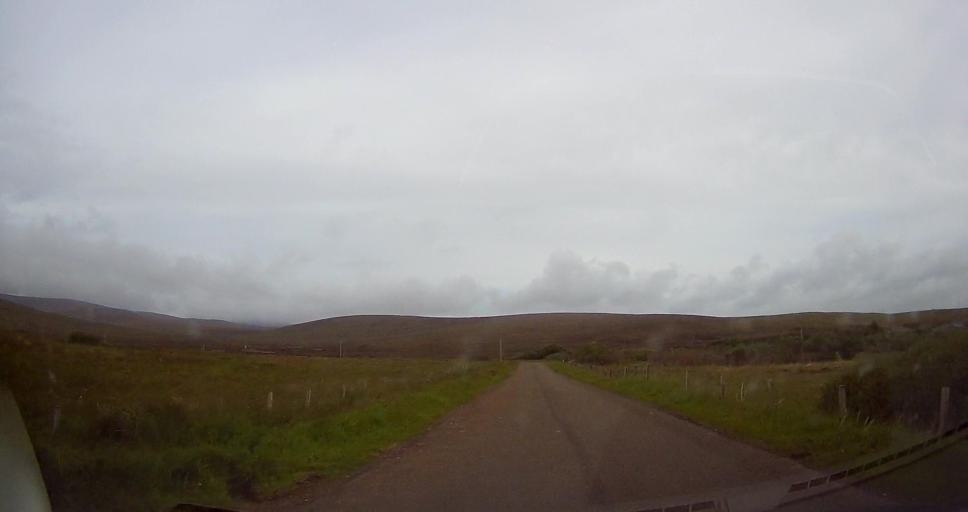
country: GB
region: Scotland
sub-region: Orkney Islands
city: Stromness
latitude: 58.8378
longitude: -3.2157
